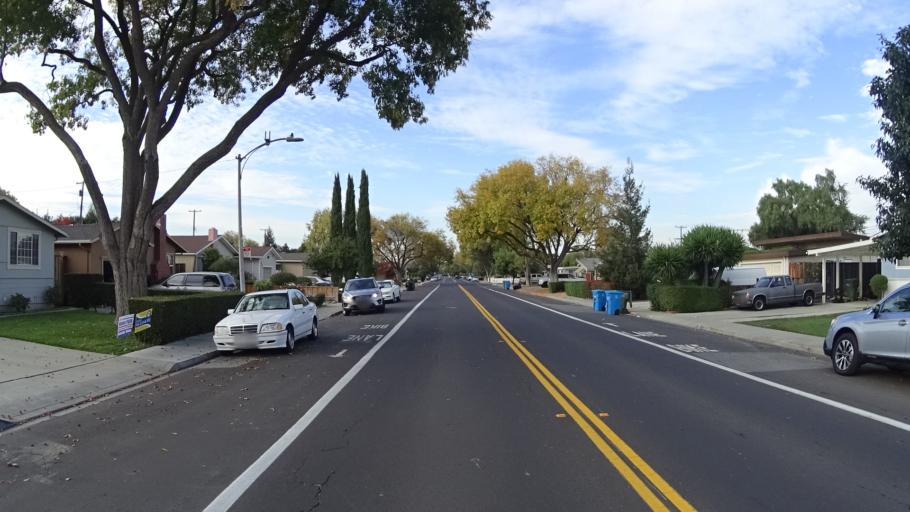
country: US
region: California
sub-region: Santa Clara County
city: Santa Clara
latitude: 37.3392
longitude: -121.9626
